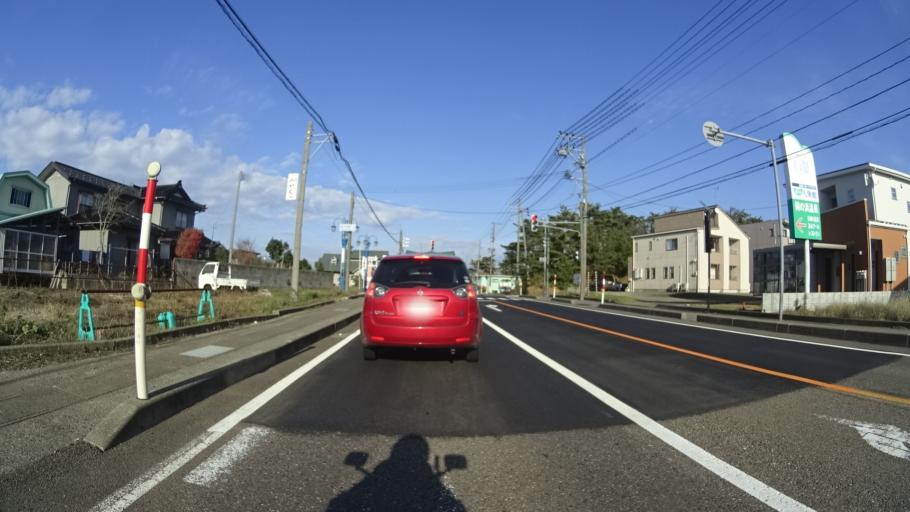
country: JP
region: Niigata
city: Joetsu
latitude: 37.2357
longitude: 138.3398
